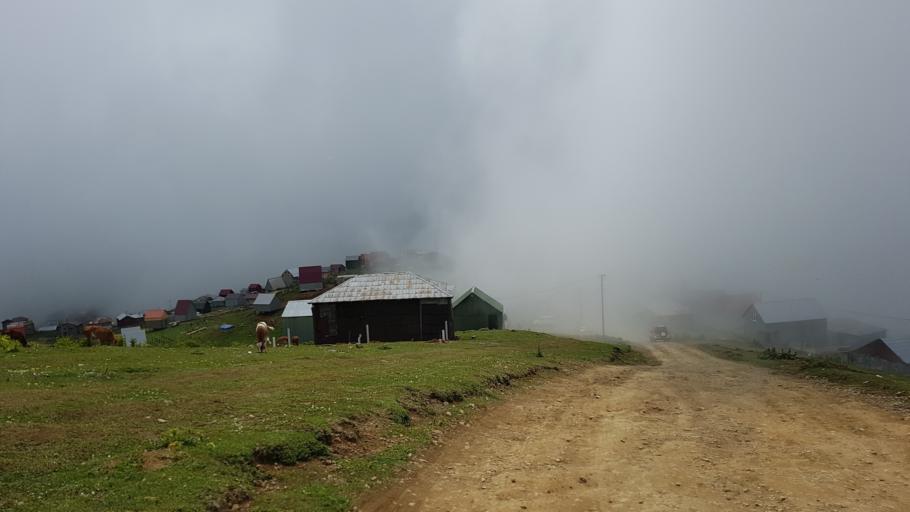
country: GE
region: Ajaria
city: Akhaldaba
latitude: 41.8260
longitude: 42.1582
